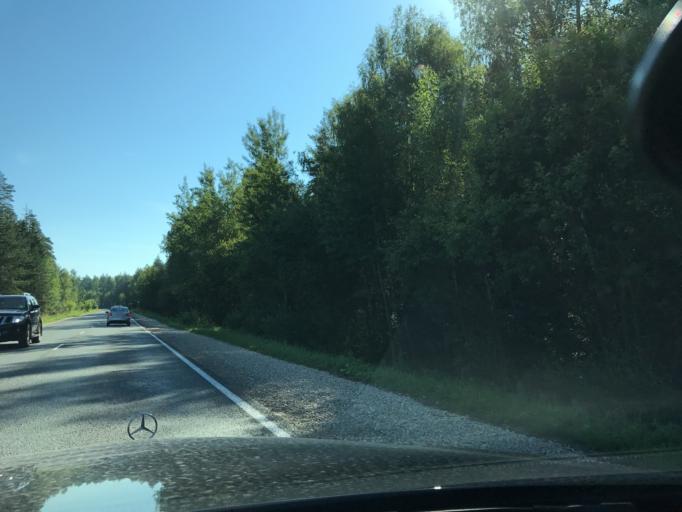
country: RU
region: Vladimir
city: Kirzhach
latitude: 56.1128
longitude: 38.7385
